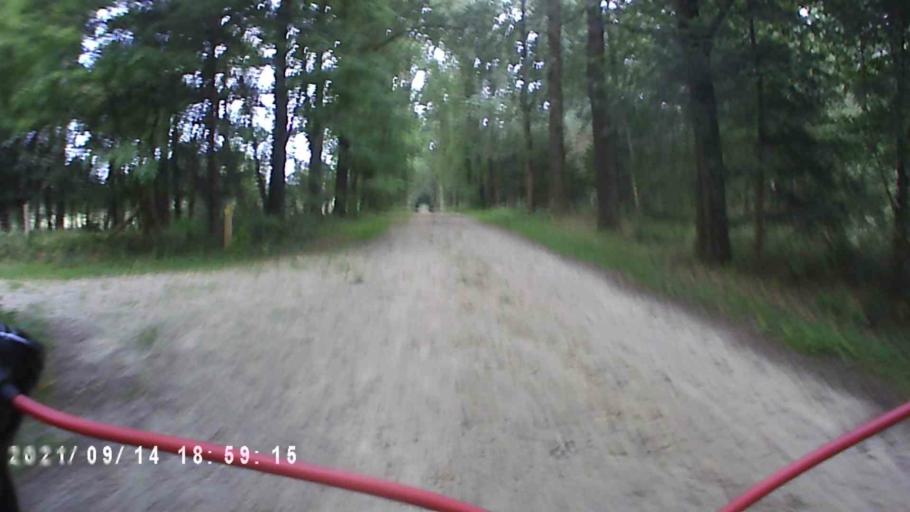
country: NL
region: Drenthe
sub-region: Gemeente Aa en Hunze
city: Anloo
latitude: 53.0322
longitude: 6.7197
